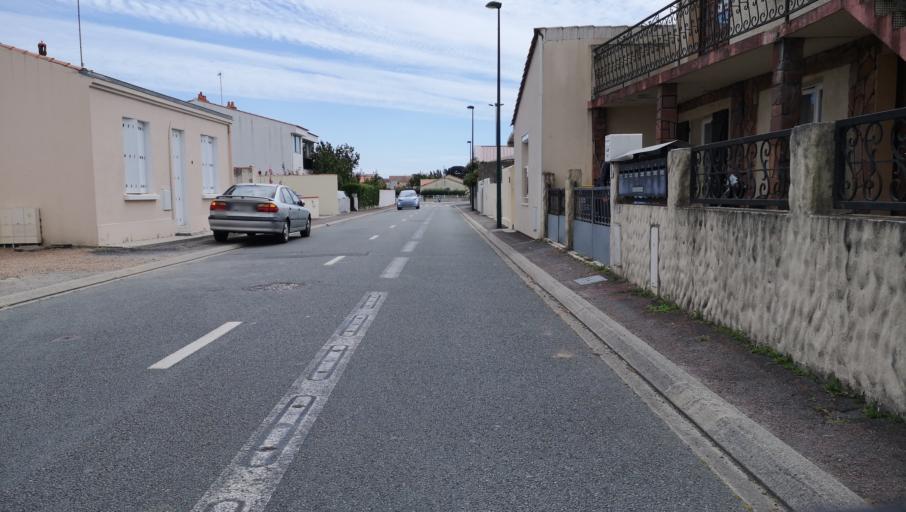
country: FR
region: Pays de la Loire
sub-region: Departement de la Vendee
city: Les Sables-d'Olonne
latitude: 46.5086
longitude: -1.7733
